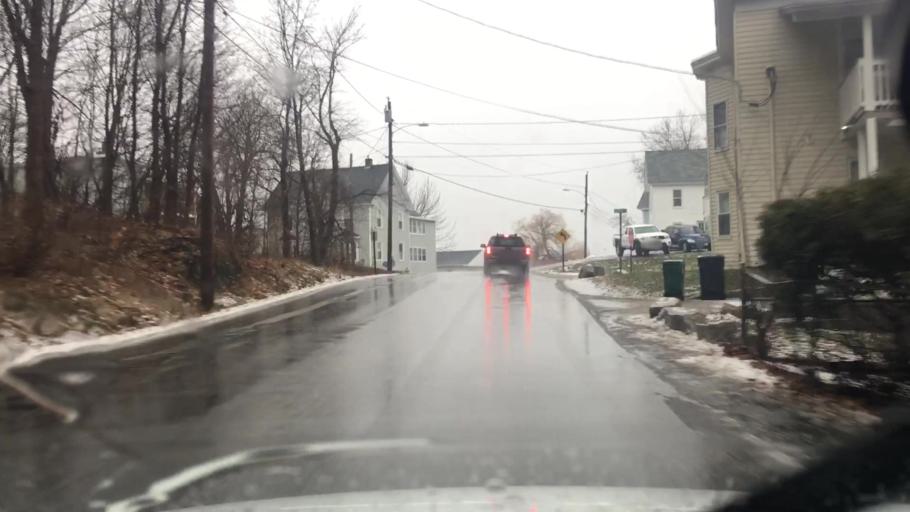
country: US
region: Maine
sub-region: York County
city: Biddeford
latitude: 43.4891
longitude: -70.4452
